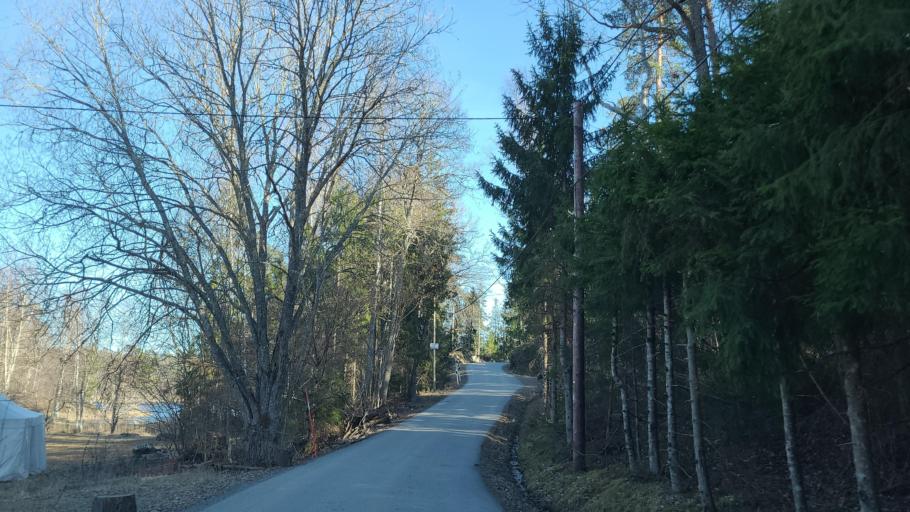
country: SE
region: Stockholm
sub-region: Varmdo Kommun
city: Holo
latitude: 59.3627
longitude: 18.6548
